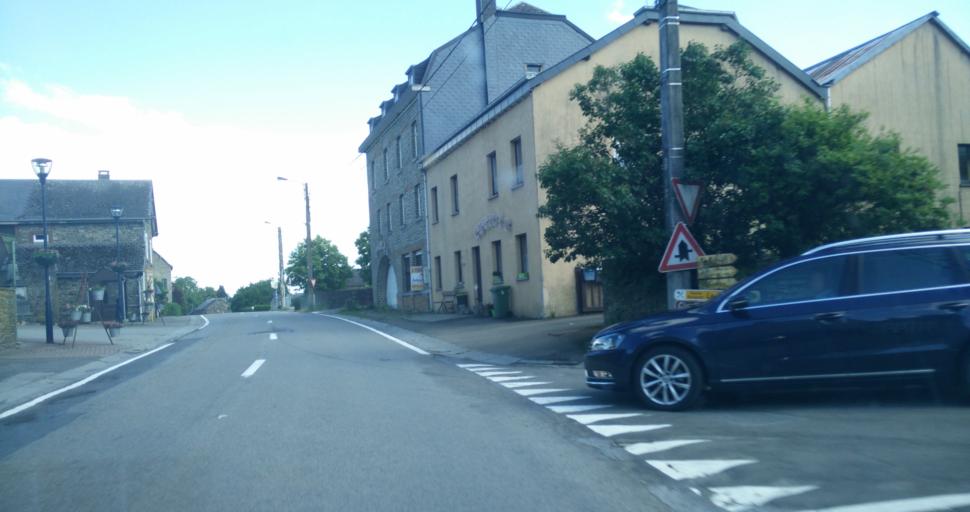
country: BE
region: Wallonia
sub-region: Province du Luxembourg
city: La Roche-en-Ardenne
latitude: 50.1785
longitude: 5.6639
